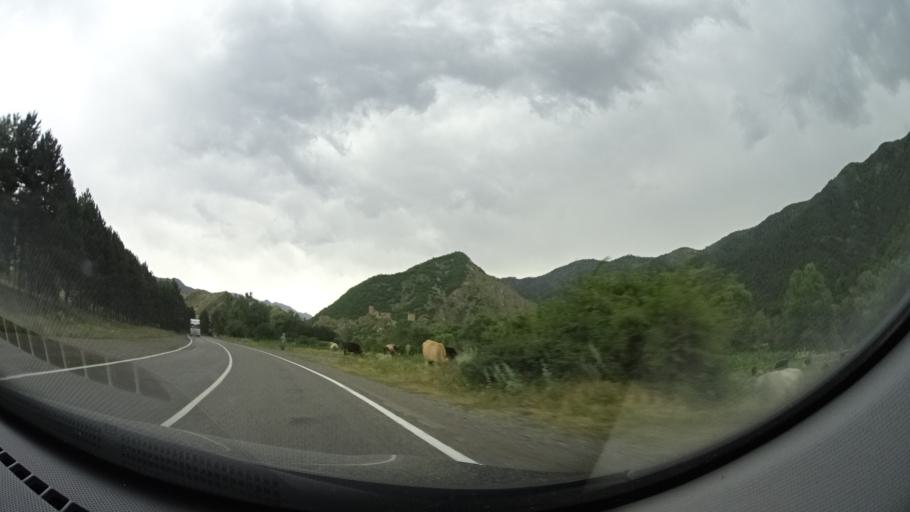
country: GE
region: Samtskhe-Javakheti
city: Aspindza
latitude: 41.7448
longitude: 43.1994
